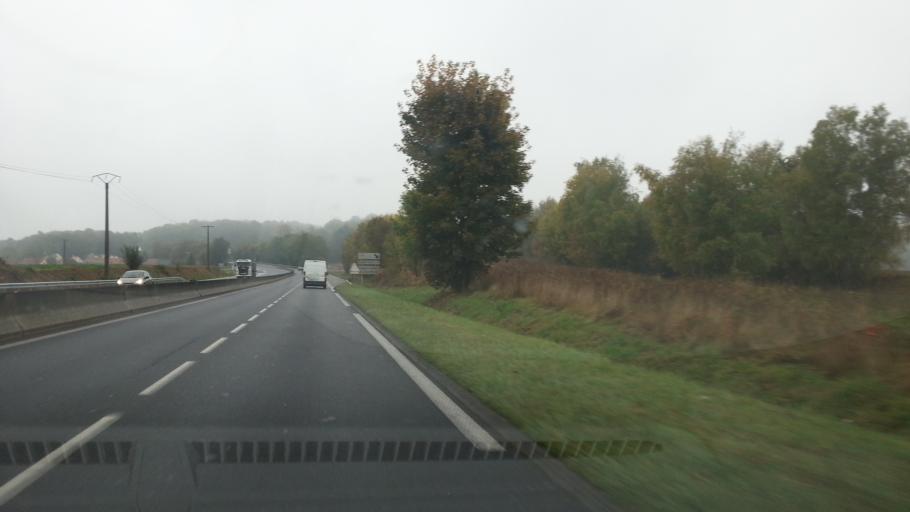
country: FR
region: Picardie
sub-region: Departement de l'Oise
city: Rantigny
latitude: 49.3344
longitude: 2.4341
